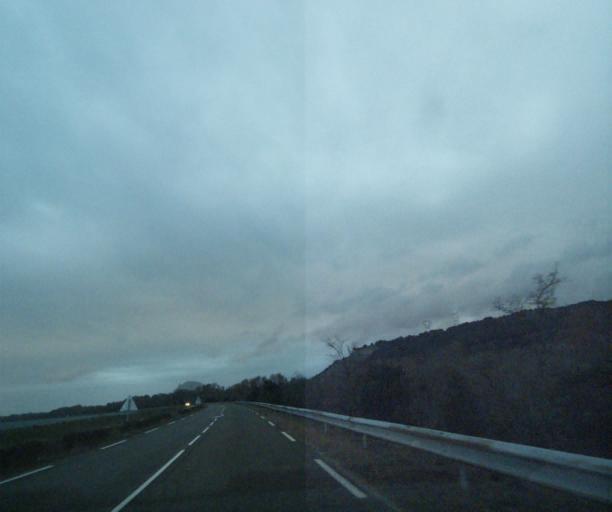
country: FR
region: Rhone-Alpes
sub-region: Departement de l'Ardeche
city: Cornas
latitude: 44.9816
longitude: 4.8564
